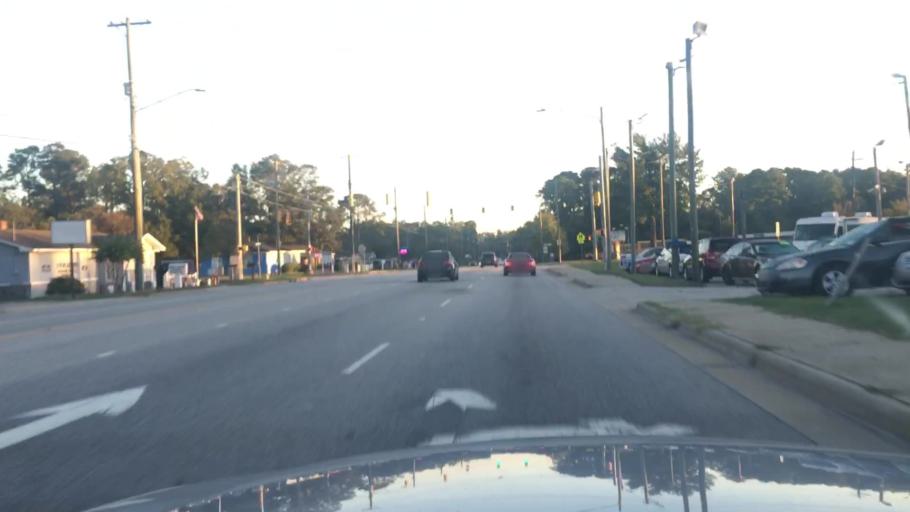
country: US
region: North Carolina
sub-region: Cumberland County
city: Hope Mills
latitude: 35.0168
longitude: -78.9638
